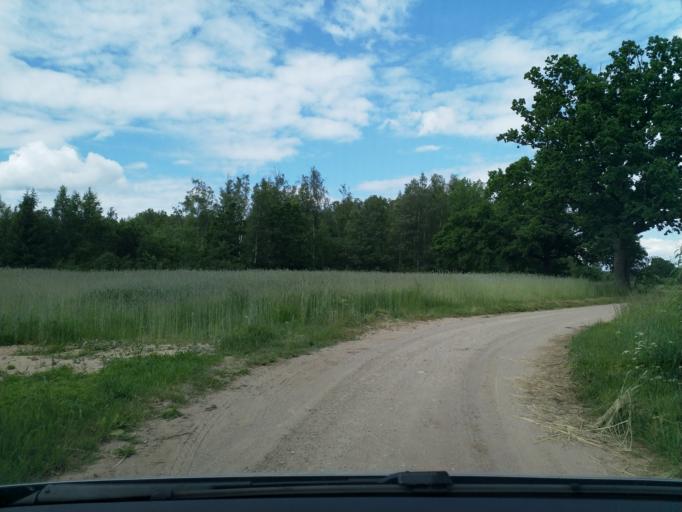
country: LV
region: Kuldigas Rajons
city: Kuldiga
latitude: 56.8349
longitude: 21.9547
